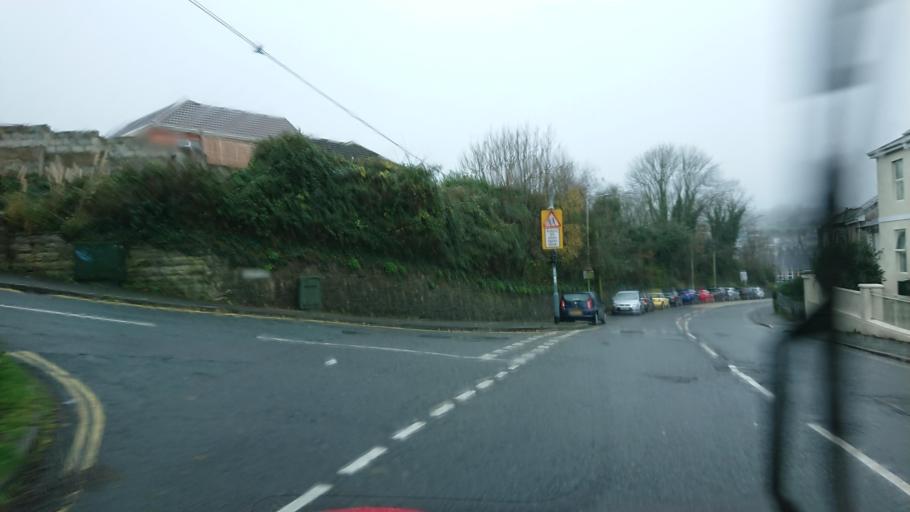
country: GB
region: England
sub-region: Plymouth
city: Plymstock
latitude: 50.3525
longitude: -4.1094
